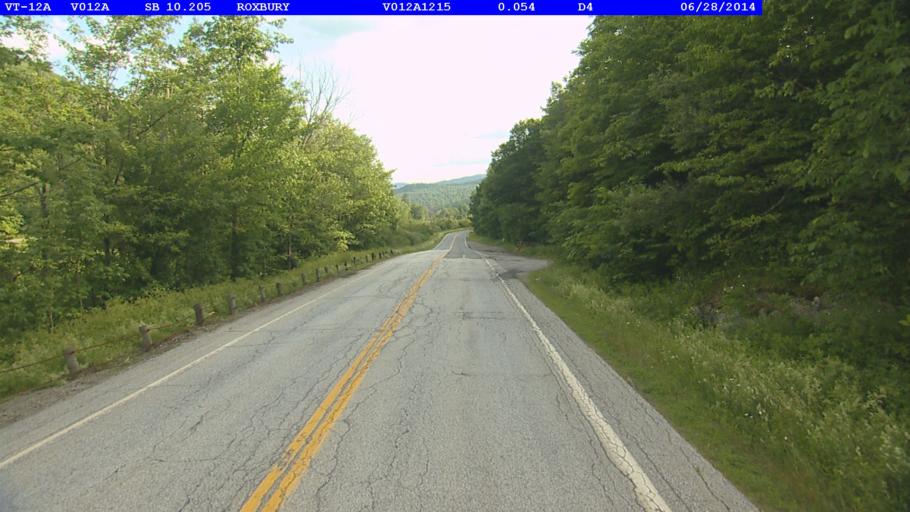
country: US
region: Vermont
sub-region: Orange County
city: Randolph
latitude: 44.0345
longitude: -72.7558
